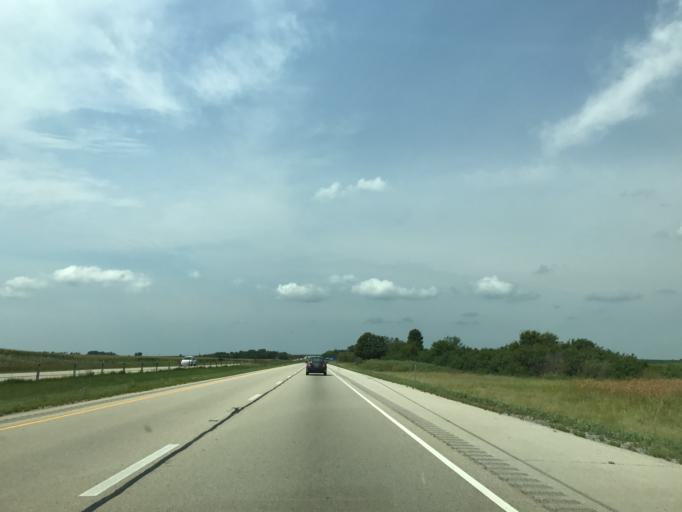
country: US
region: Illinois
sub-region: LaSalle County
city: Marseilles
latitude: 41.3757
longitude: -88.6615
